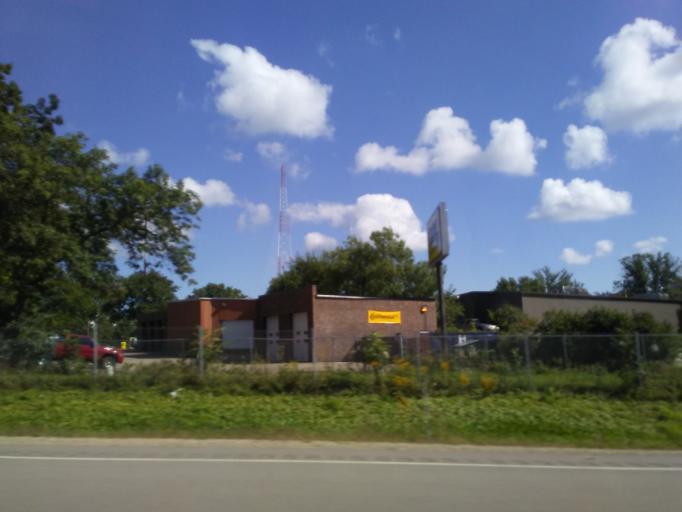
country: US
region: Wisconsin
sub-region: Dane County
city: Shorewood Hills
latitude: 43.0490
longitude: -89.4790
